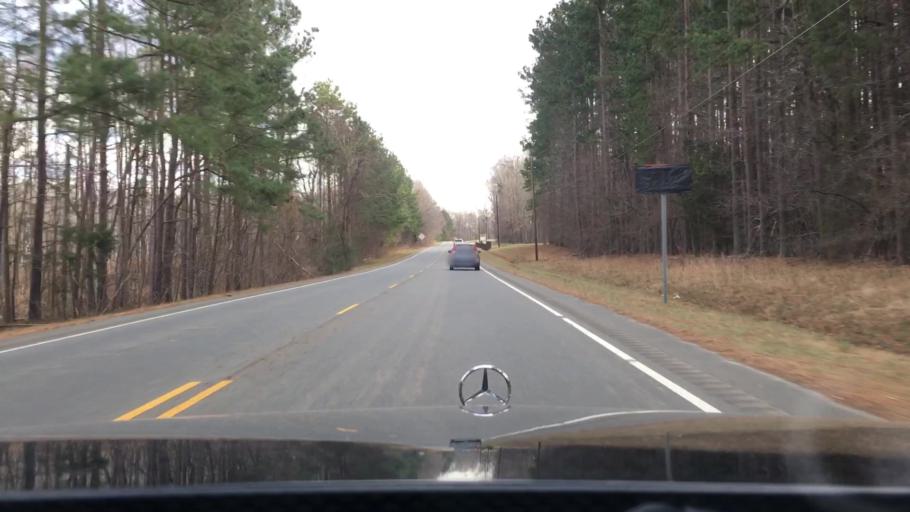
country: US
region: North Carolina
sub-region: Orange County
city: Hillsborough
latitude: 36.1738
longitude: -79.1338
